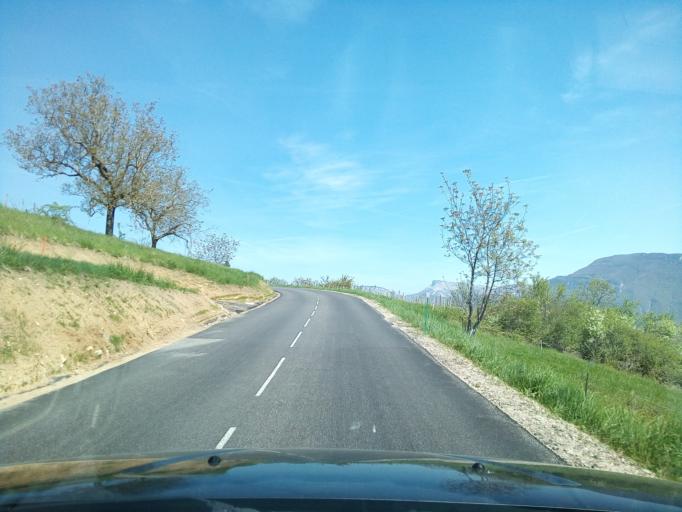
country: FR
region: Rhone-Alpes
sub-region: Departement de l'Isere
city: Chapareillan
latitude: 45.4783
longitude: 5.9762
